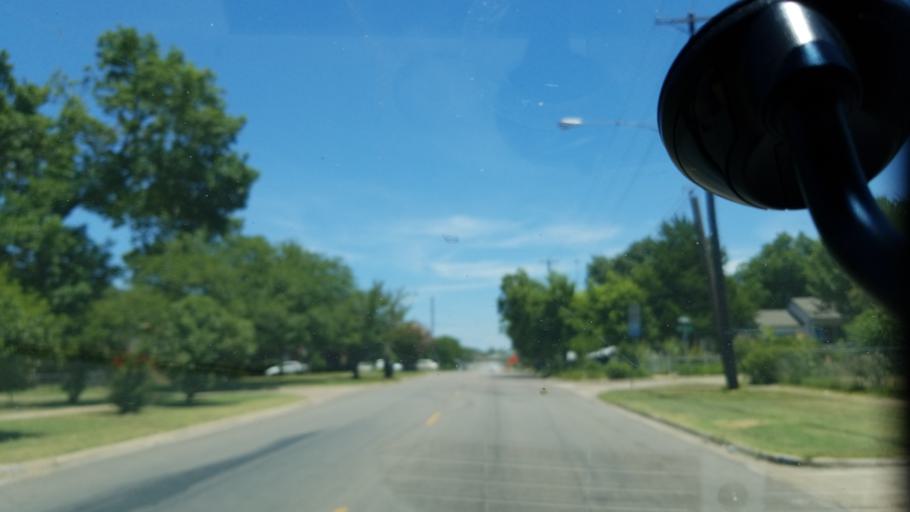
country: US
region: Texas
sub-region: Dallas County
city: Cockrell Hill
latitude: 32.7132
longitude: -96.8332
